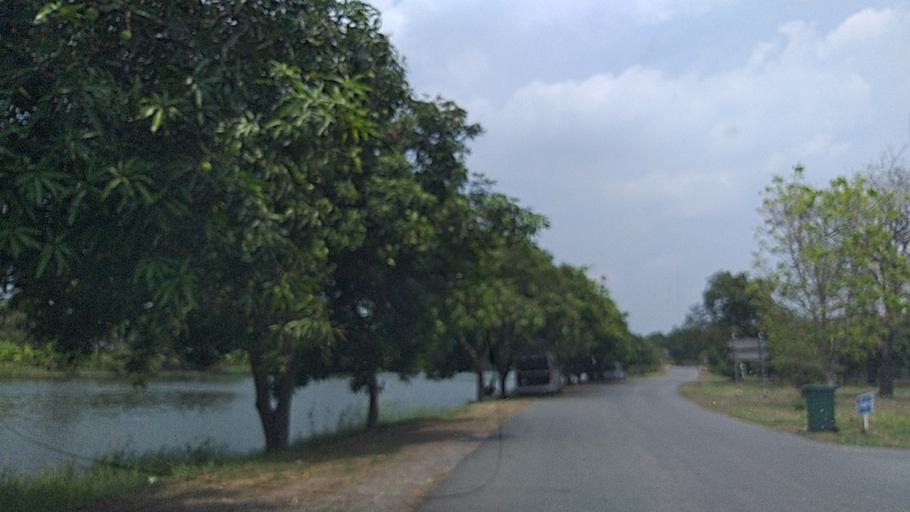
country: TH
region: Bangkok
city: Thawi Watthana
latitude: 13.7738
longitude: 100.3110
